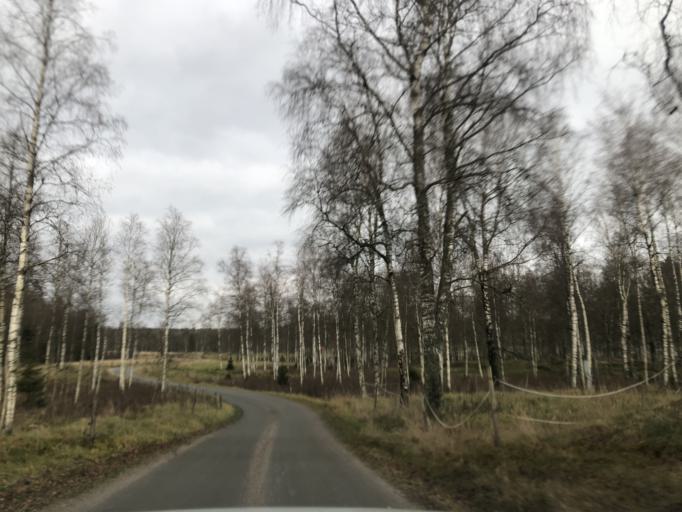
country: SE
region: Vaestra Goetaland
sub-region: Boras Kommun
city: Dalsjofors
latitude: 57.8315
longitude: 13.1736
